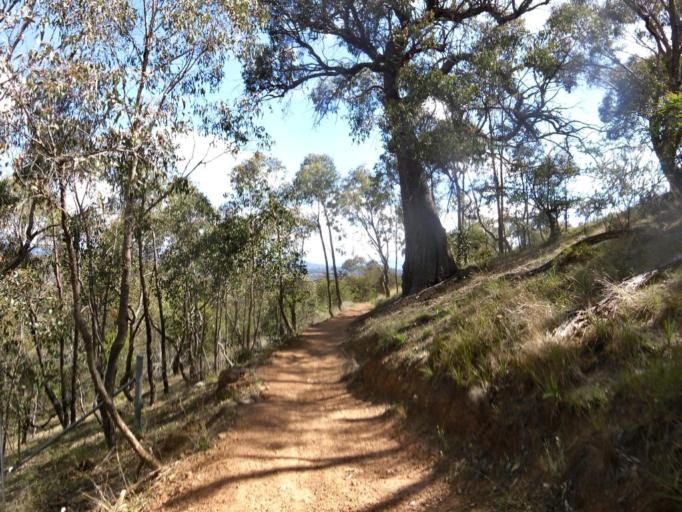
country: AU
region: Australian Capital Territory
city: Belconnen
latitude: -35.1546
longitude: 149.0843
